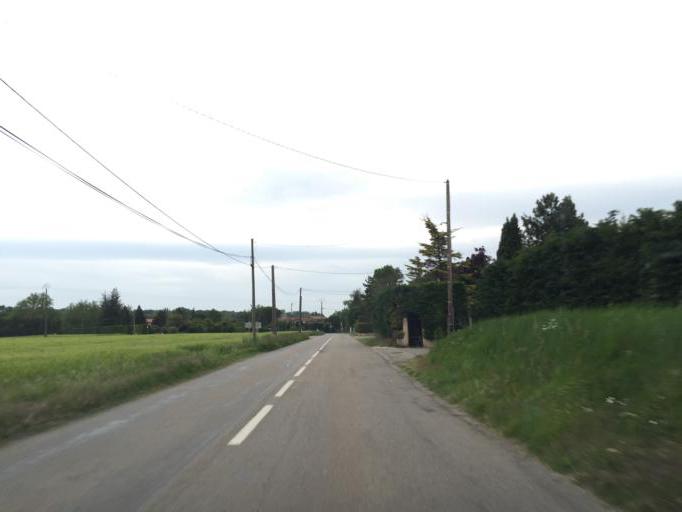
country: FR
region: Rhone-Alpes
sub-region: Departement de la Drome
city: Chabeuil
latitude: 44.9127
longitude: 5.0377
